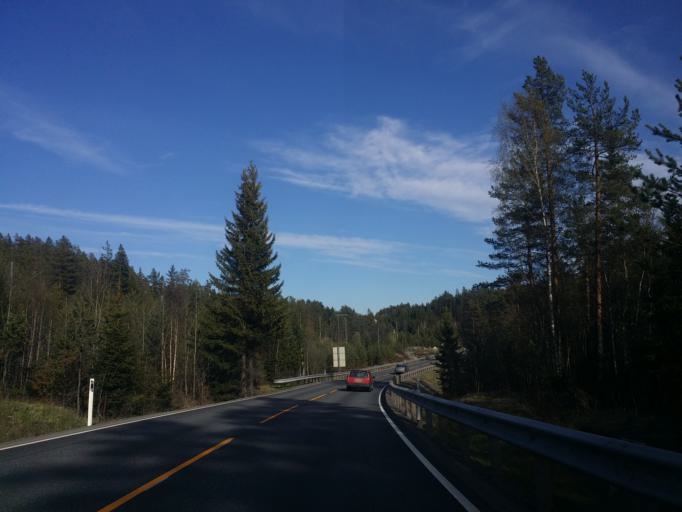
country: NO
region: Buskerud
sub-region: Kongsberg
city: Kongsberg
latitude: 59.6303
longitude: 9.5396
